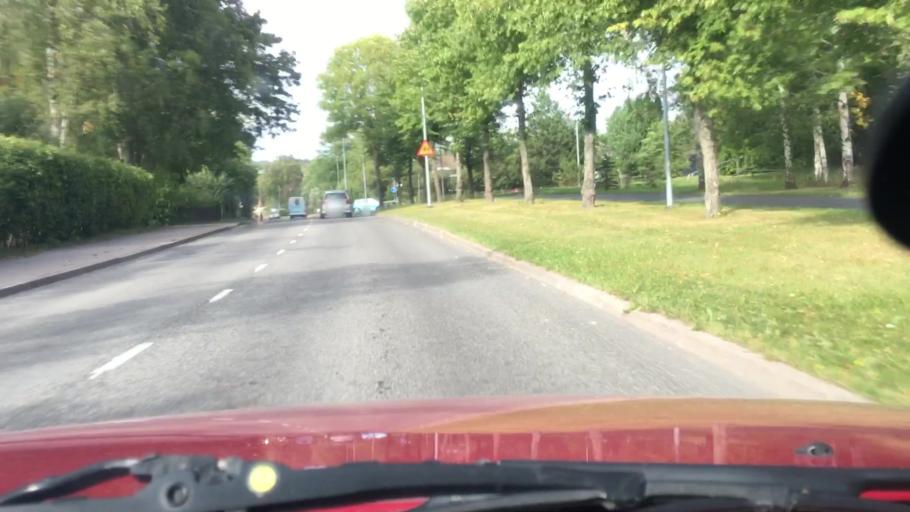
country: FI
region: Varsinais-Suomi
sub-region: Turku
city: Turku
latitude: 60.4573
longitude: 22.2457
